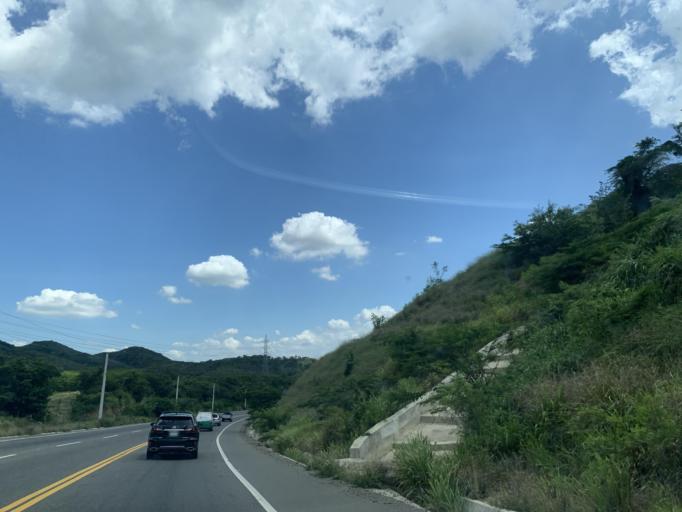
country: DO
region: Santiago
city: Villa Bisono
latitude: 19.6047
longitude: -70.8376
